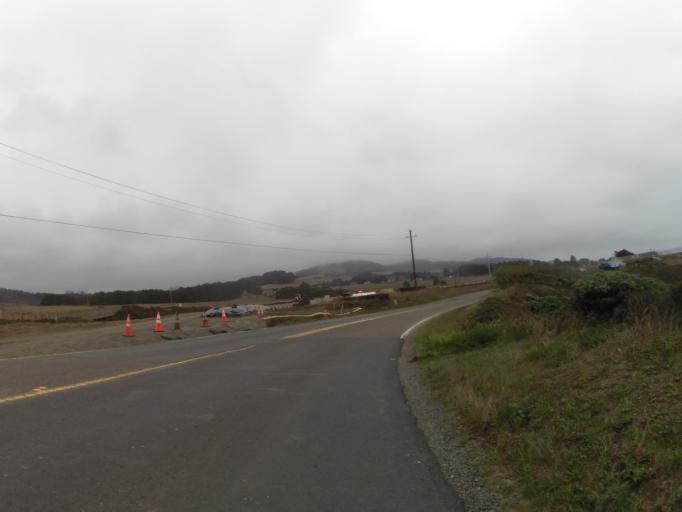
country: US
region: California
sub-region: Sonoma County
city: Bodega Bay
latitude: 38.3913
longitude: -123.0861
